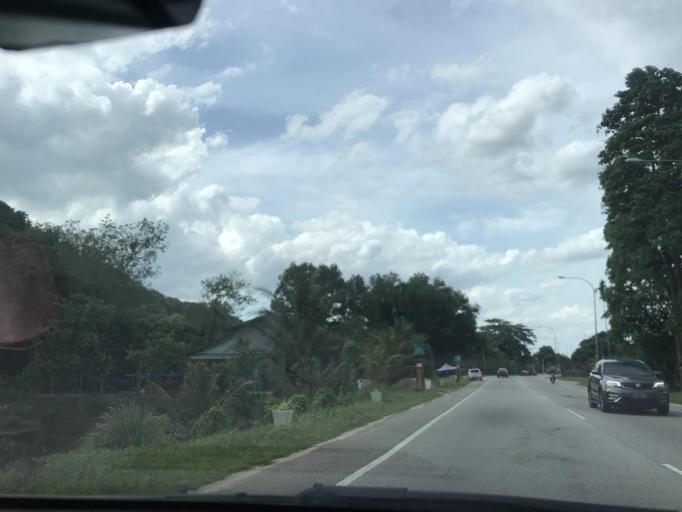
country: MY
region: Kelantan
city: Kampong Pangkal Kalong
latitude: 5.8870
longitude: 102.1788
